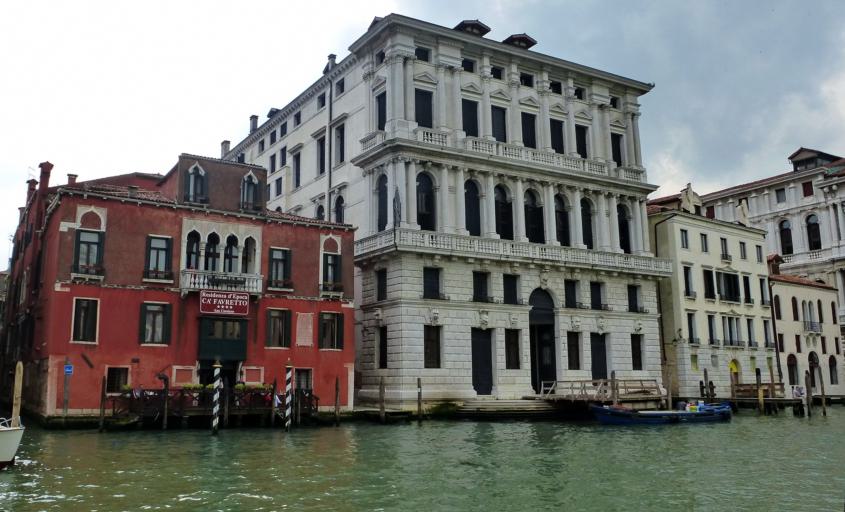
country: IT
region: Veneto
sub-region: Provincia di Venezia
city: Venice
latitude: 45.4407
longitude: 12.3327
